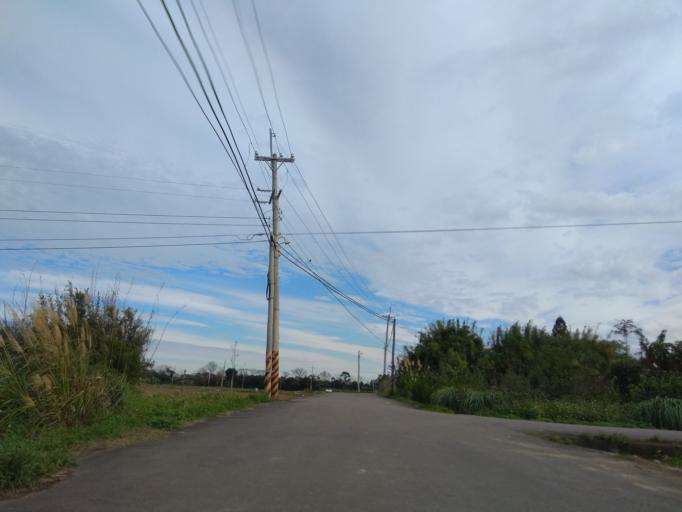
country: TW
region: Taiwan
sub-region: Hsinchu
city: Zhubei
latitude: 24.9498
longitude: 121.1097
